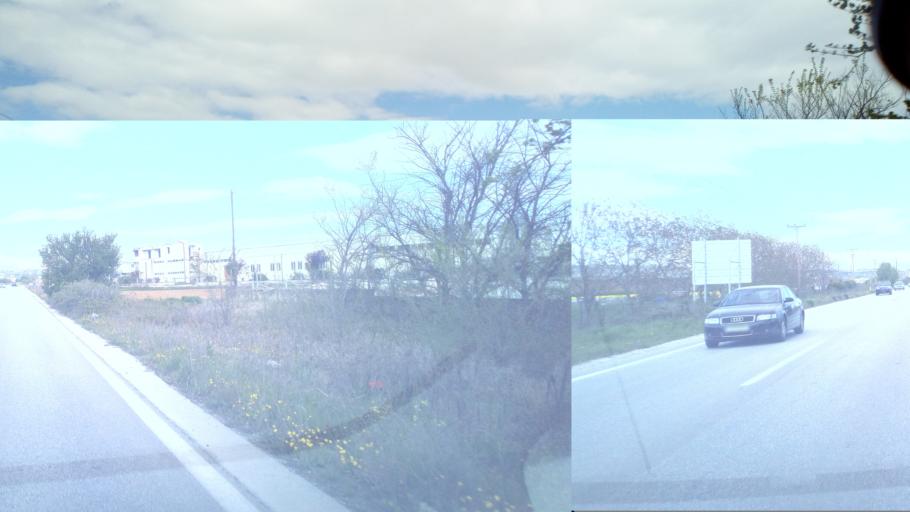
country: GR
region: Central Macedonia
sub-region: Nomos Thessalonikis
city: Drymos
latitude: 40.7621
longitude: 22.9664
